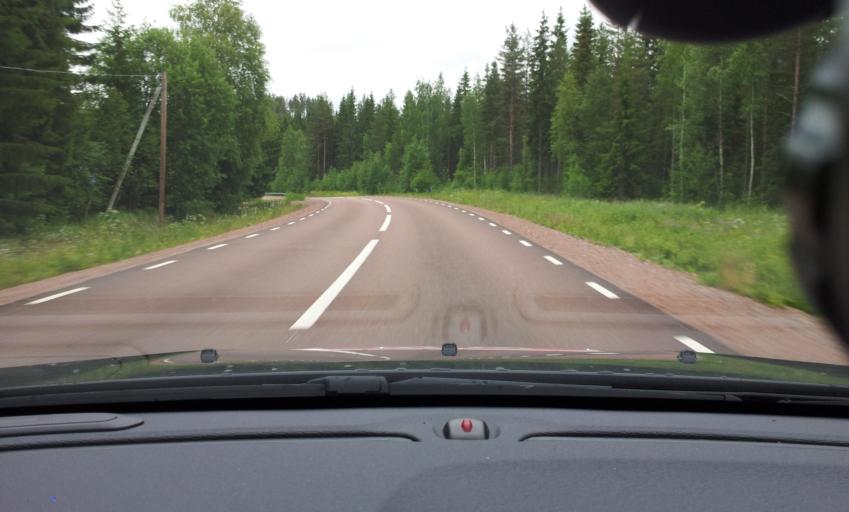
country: SE
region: Jaemtland
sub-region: Ragunda Kommun
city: Hammarstrand
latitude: 63.0229
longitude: 16.5406
